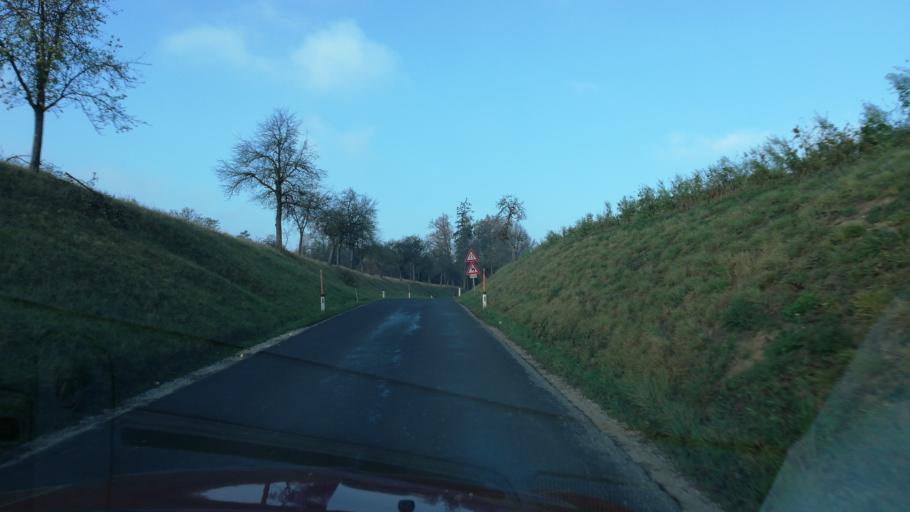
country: AT
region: Upper Austria
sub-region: Politischer Bezirk Kirchdorf an der Krems
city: Kremsmunster
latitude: 48.1154
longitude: 14.1562
